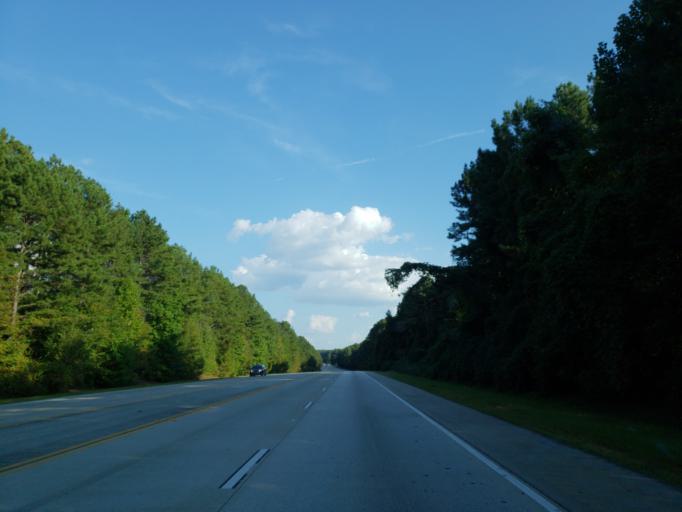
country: US
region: Georgia
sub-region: Cobb County
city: Powder Springs
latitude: 33.8391
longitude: -84.6837
